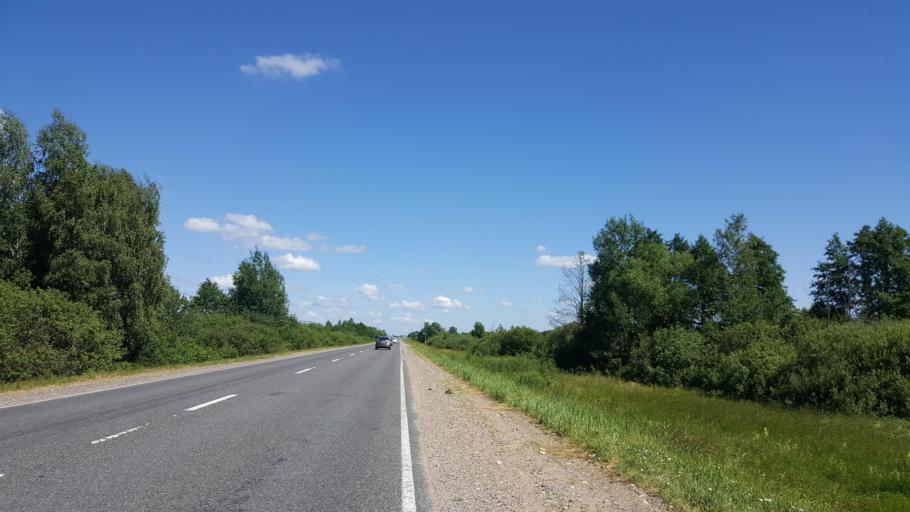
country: BY
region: Brest
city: Kamyanyets
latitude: 52.3892
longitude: 23.7869
